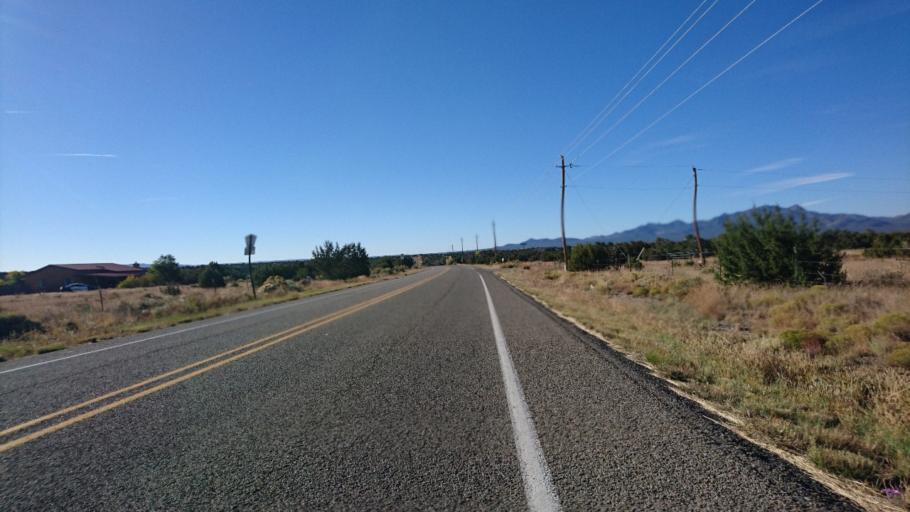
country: US
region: New Mexico
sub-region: Santa Fe County
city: La Cienega
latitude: 35.4647
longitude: -106.0701
